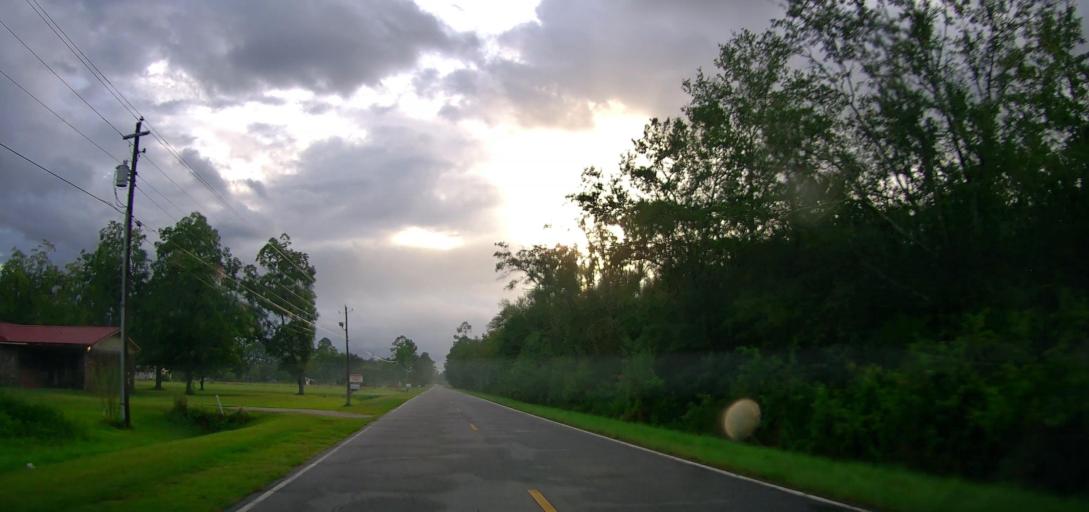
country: US
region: Georgia
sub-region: Ware County
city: Deenwood
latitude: 31.1950
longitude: -82.3958
